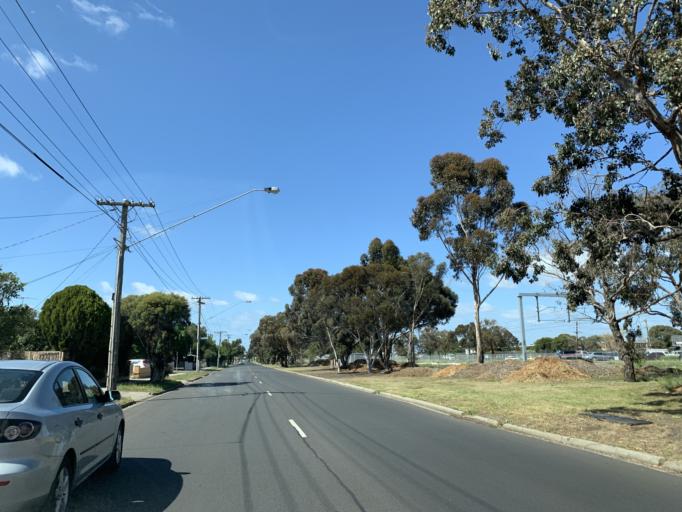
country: AU
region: Victoria
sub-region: Brimbank
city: Saint Albans
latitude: -37.7364
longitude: 144.7964
